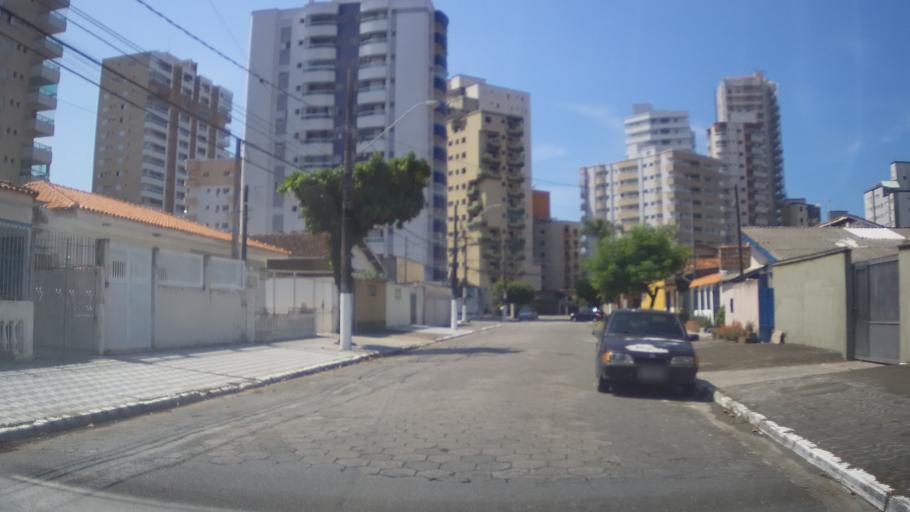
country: BR
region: Sao Paulo
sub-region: Praia Grande
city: Praia Grande
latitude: -24.0102
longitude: -46.4260
